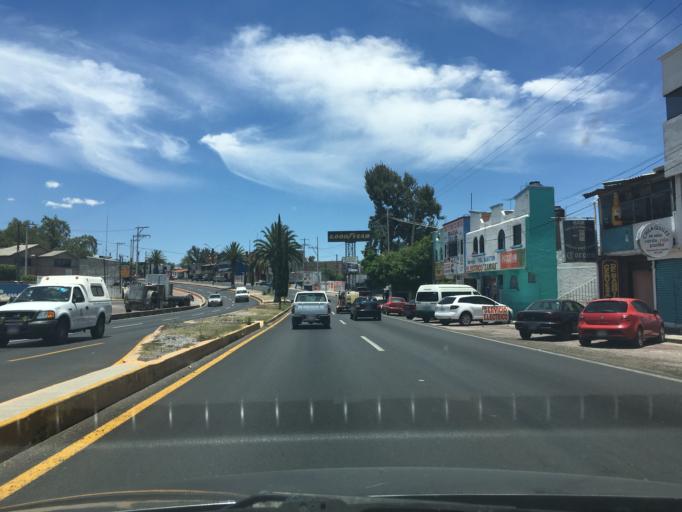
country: MX
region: Hidalgo
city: Actopan
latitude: 20.2641
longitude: -98.9468
